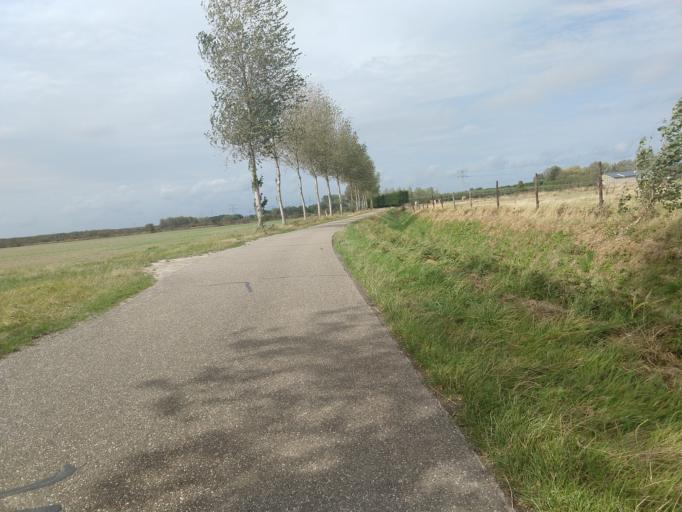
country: NL
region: Zeeland
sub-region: Gemeente Reimerswaal
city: Yerseke
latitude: 51.4540
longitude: 3.9994
